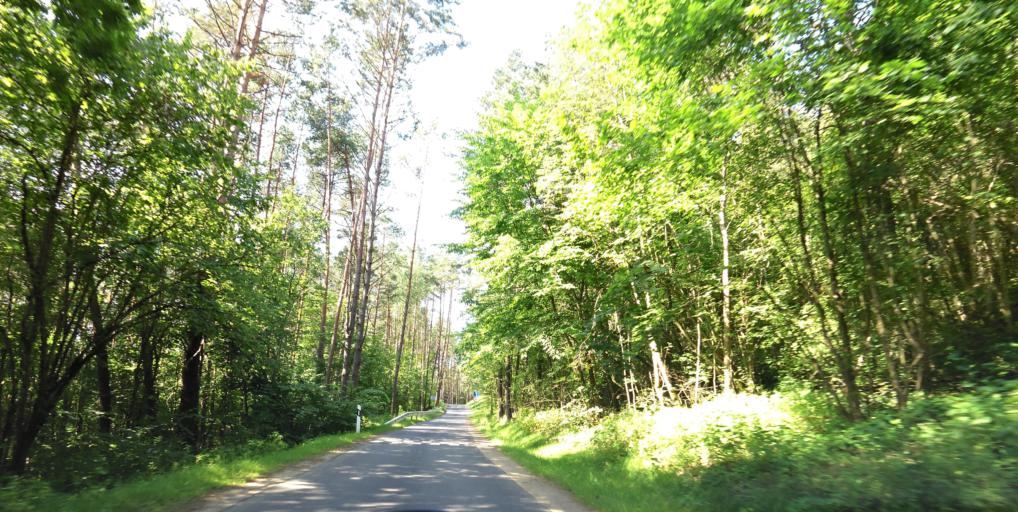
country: LT
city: Grigiskes
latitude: 54.7255
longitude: 25.0605
